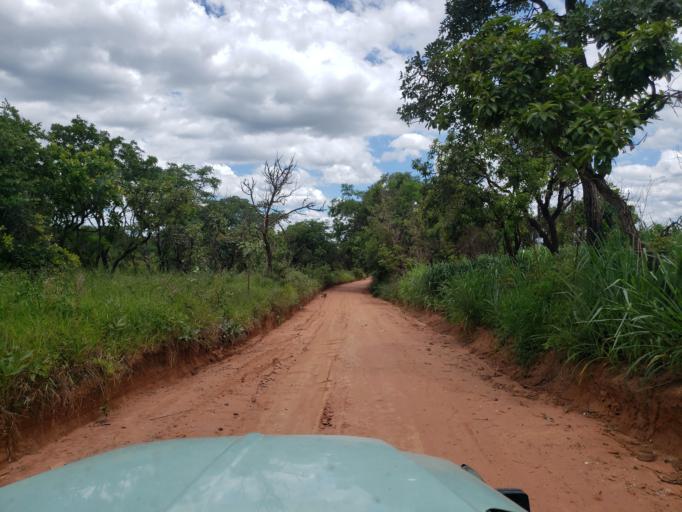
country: BR
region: Sao Paulo
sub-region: Aguai
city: Aguai
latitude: -22.1887
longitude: -46.9501
